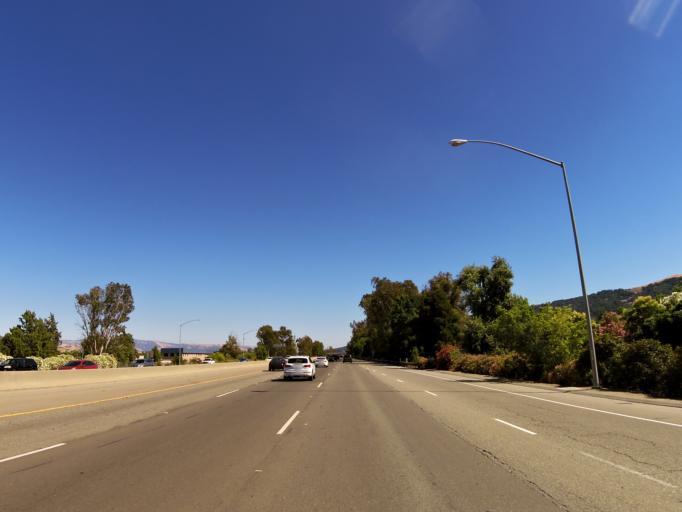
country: US
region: California
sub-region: Alameda County
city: Dublin
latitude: 37.6878
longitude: -121.9177
